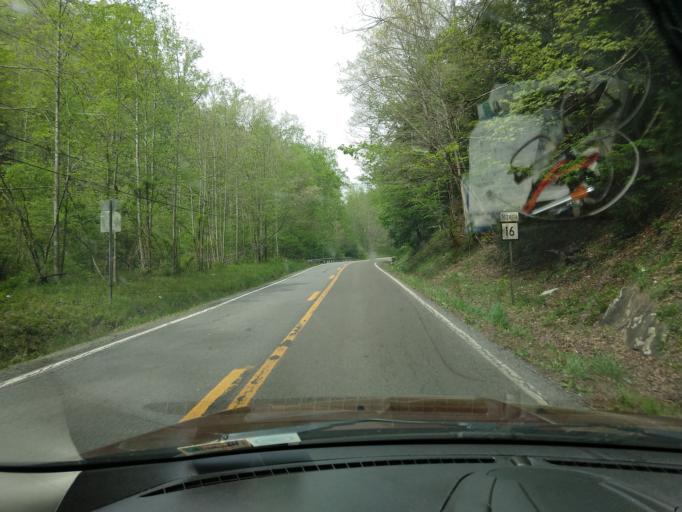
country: US
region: West Virginia
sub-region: McDowell County
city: Welch
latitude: 37.3444
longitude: -81.6698
